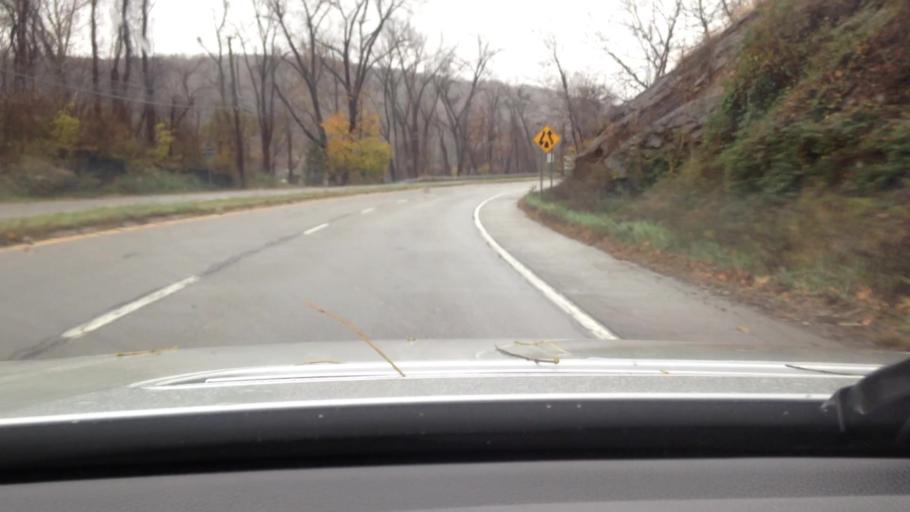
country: US
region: New York
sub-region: Westchester County
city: Peekskill
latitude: 41.3052
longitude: -73.9296
